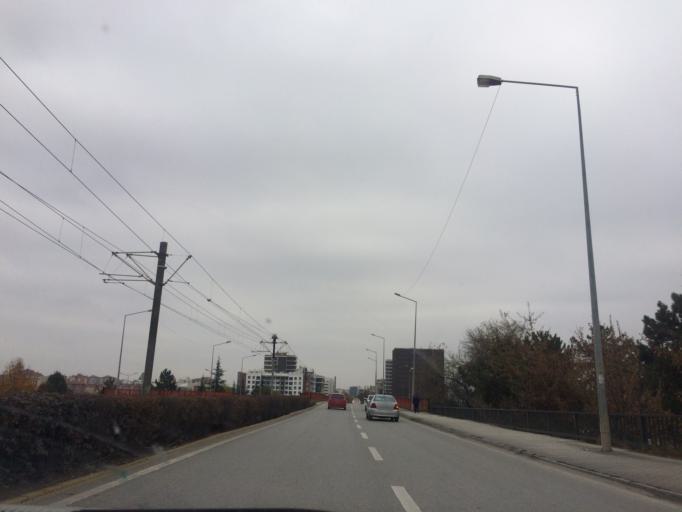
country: TR
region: Eskisehir
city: Eskisehir
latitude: 39.7877
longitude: 30.4954
